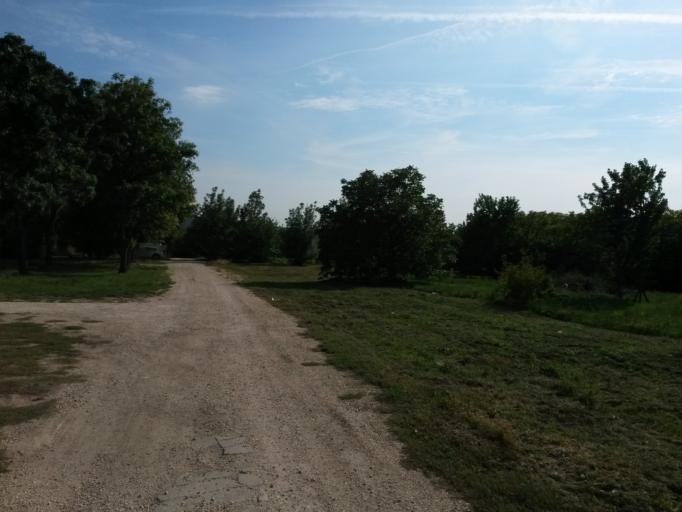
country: HU
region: Pest
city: Budaors
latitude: 47.4645
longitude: 18.9865
